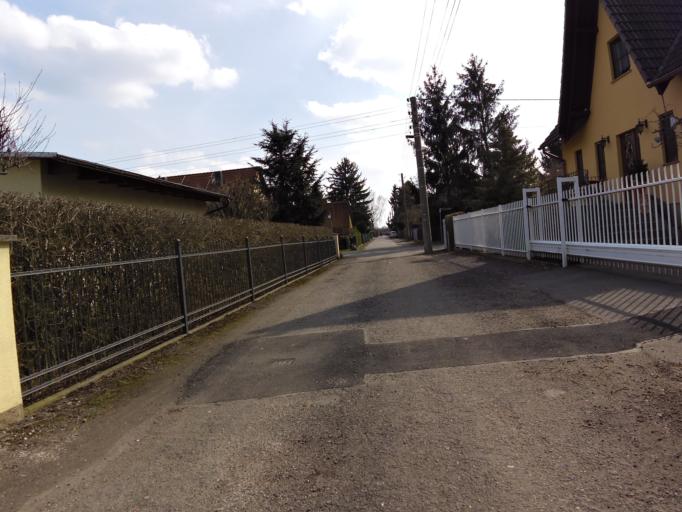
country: DE
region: Saxony
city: Markranstadt
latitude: 51.3102
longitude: 12.2840
